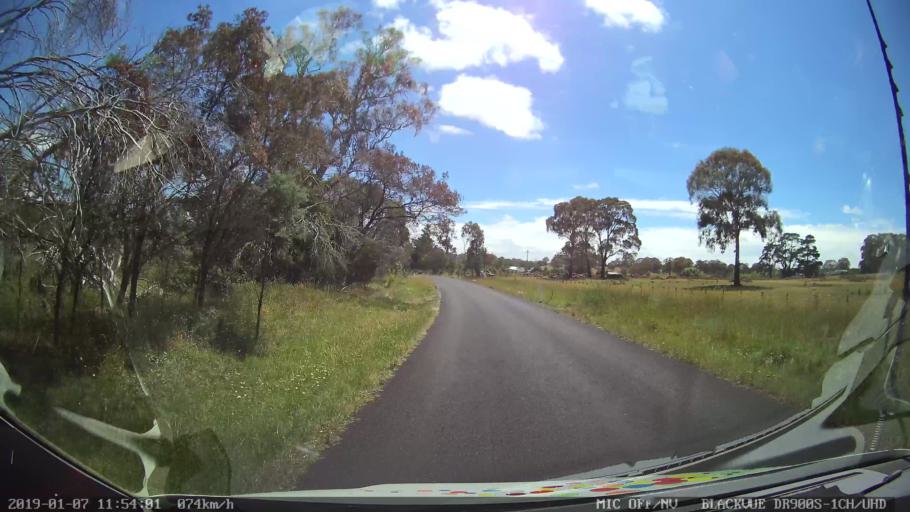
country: AU
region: New South Wales
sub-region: Guyra
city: Guyra
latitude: -30.3005
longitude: 151.6633
